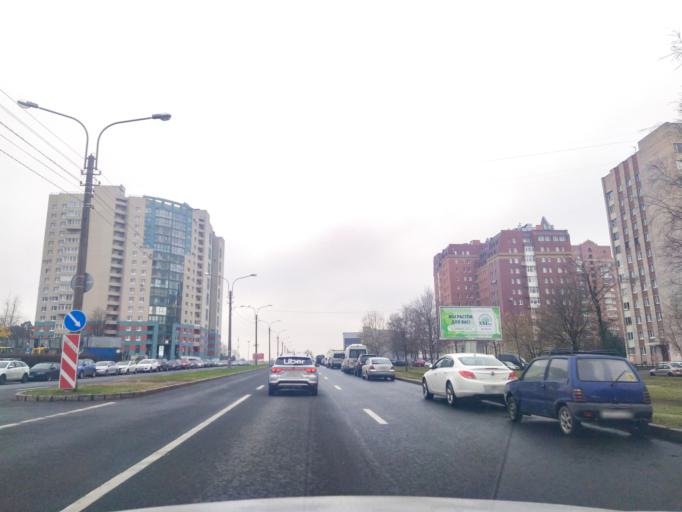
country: RU
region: Leningrad
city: Udel'naya
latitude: 60.0306
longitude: 30.3276
